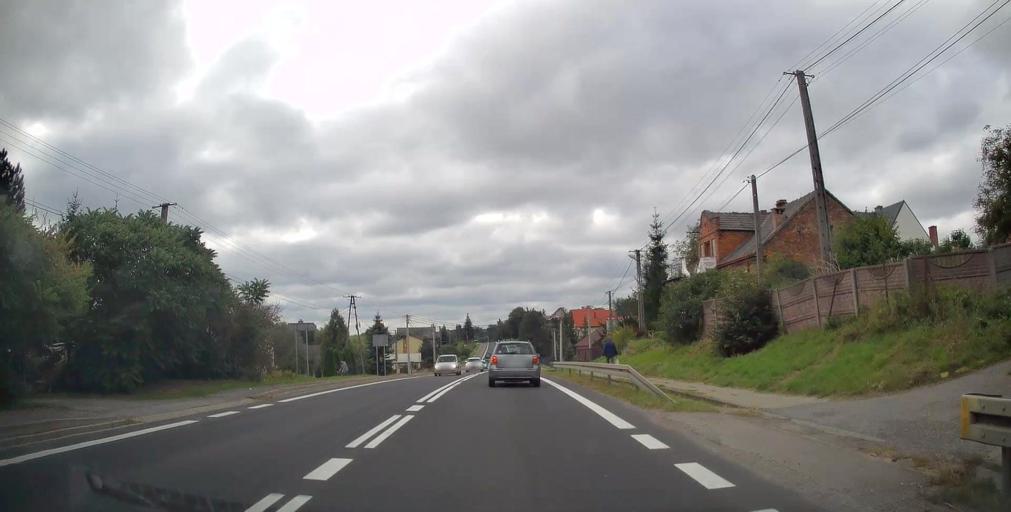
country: PL
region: Lesser Poland Voivodeship
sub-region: Powiat krakowski
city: Michalowice
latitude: 50.1704
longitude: 19.9779
